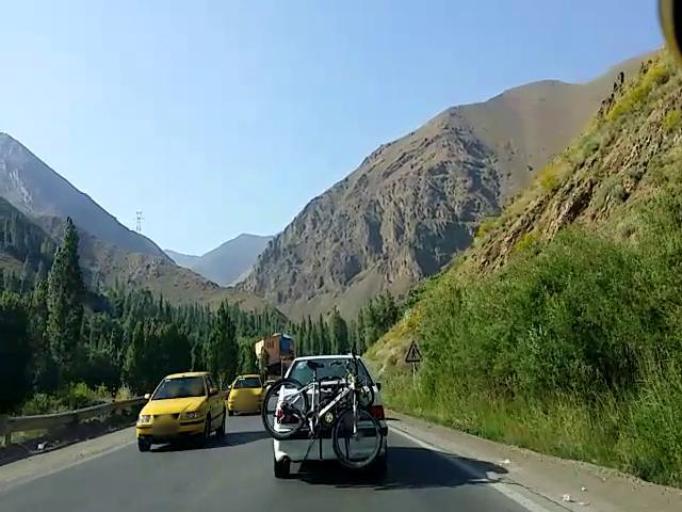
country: IR
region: Tehran
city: Tajrish
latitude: 36.1089
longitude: 51.3192
